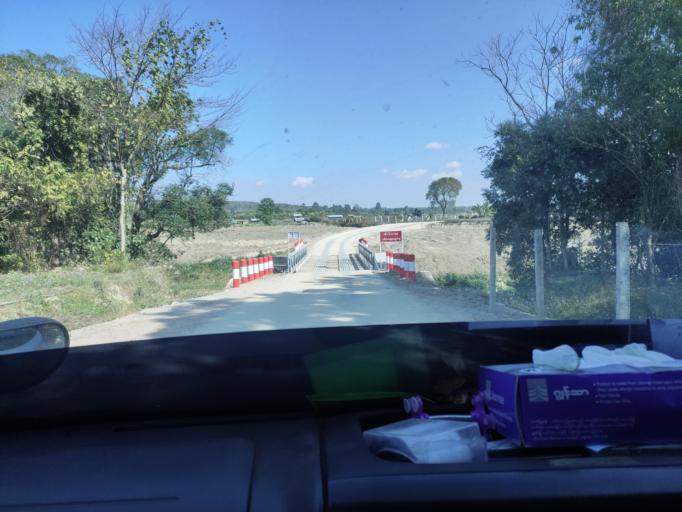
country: MM
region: Mandalay
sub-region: Pyin Oo Lwin District
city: Pyin Oo Lwin
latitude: 22.0658
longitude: 96.5306
